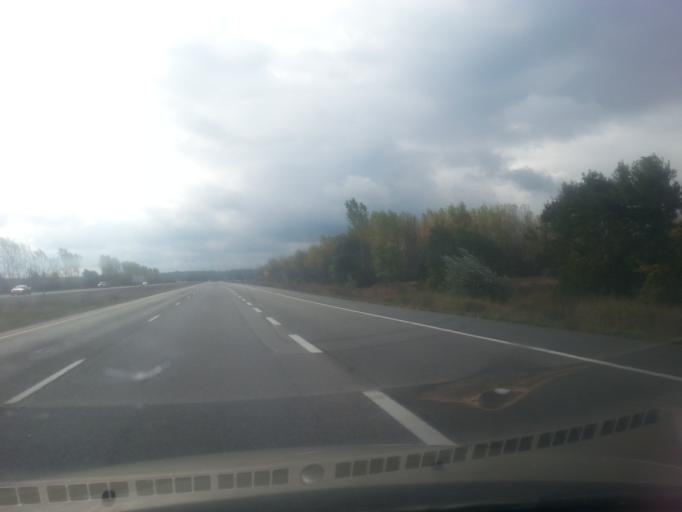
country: CA
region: Ontario
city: Bells Corners
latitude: 45.3079
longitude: -75.7977
